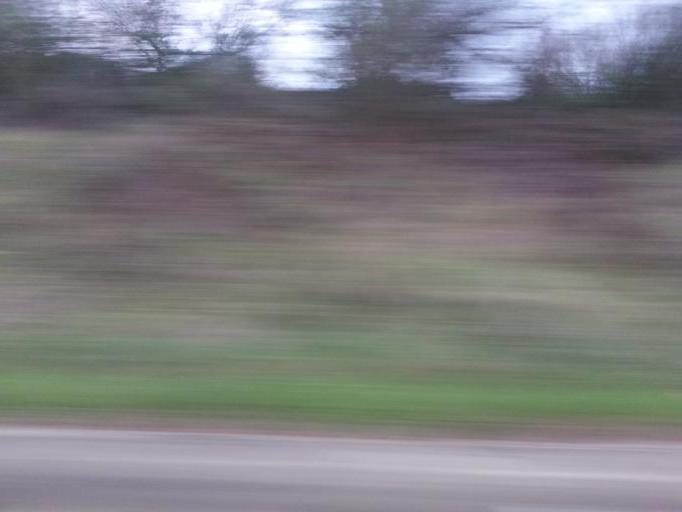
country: US
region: Tennessee
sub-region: Washington County
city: Johnson City
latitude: 36.3008
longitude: -82.3532
